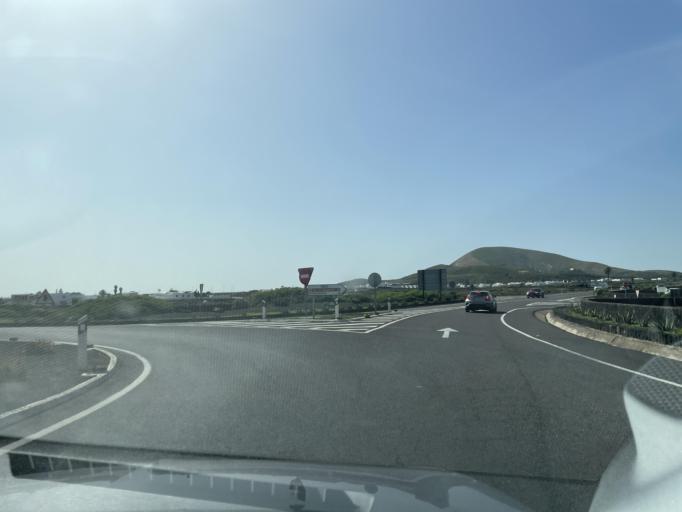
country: ES
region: Canary Islands
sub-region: Provincia de Las Palmas
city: San Bartolome
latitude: 29.0154
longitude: -13.6148
